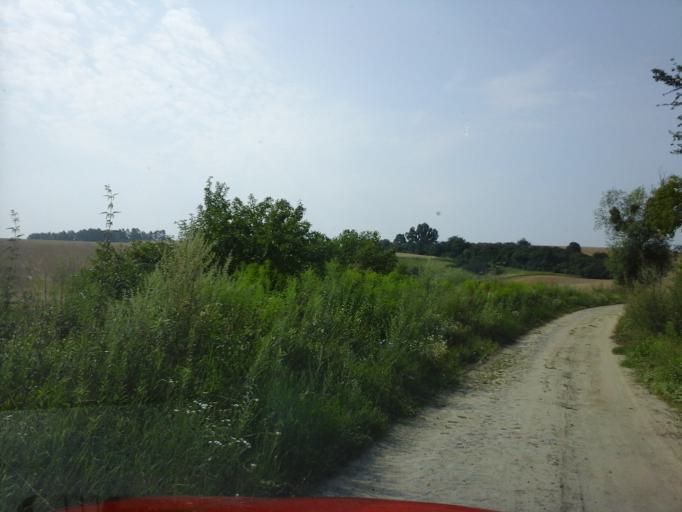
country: PL
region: West Pomeranian Voivodeship
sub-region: Powiat mysliborski
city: Barlinek
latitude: 53.0716
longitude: 15.2049
